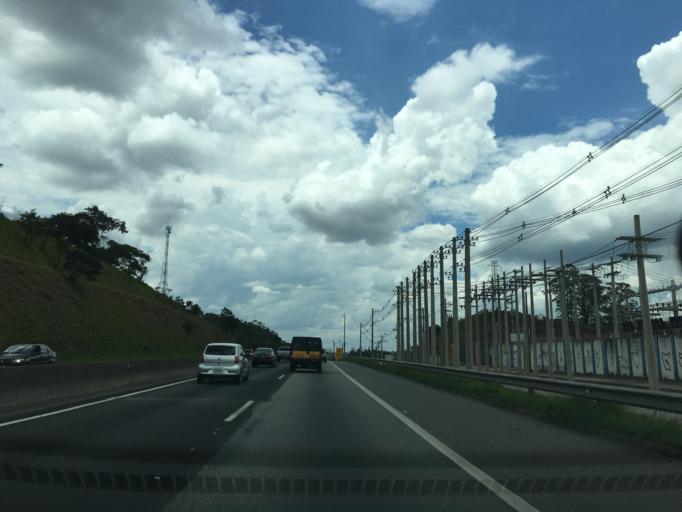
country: BR
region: Sao Paulo
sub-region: Atibaia
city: Atibaia
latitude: -23.2082
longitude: -46.5917
